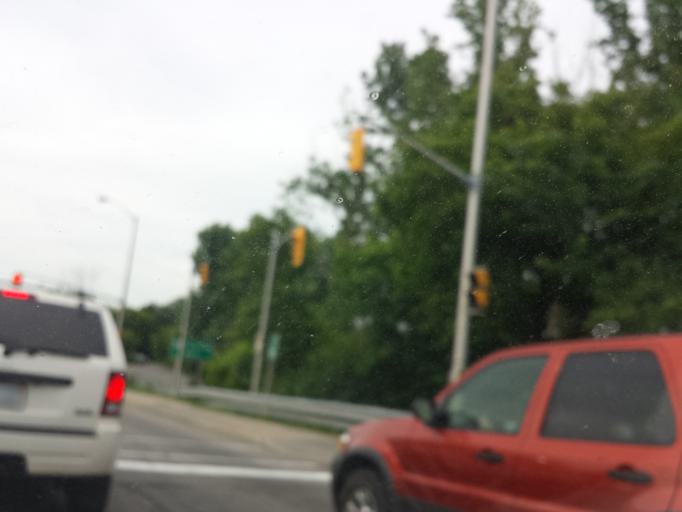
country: CA
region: Ontario
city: Ottawa
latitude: 45.3712
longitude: -75.7550
